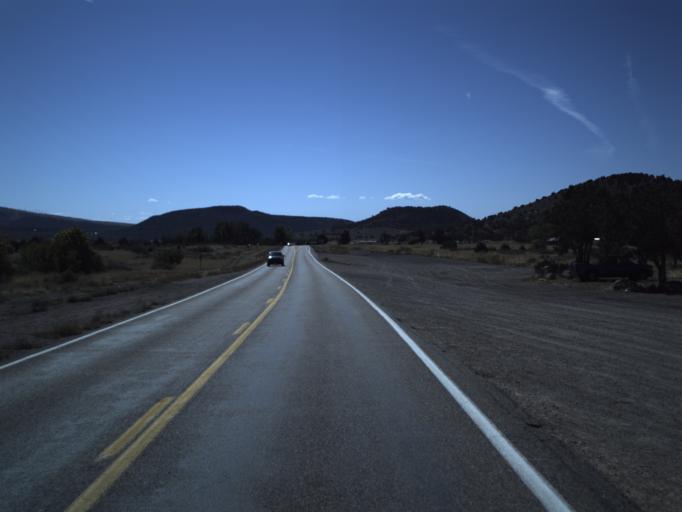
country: US
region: Utah
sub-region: Washington County
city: Enterprise
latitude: 37.4210
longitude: -113.6313
